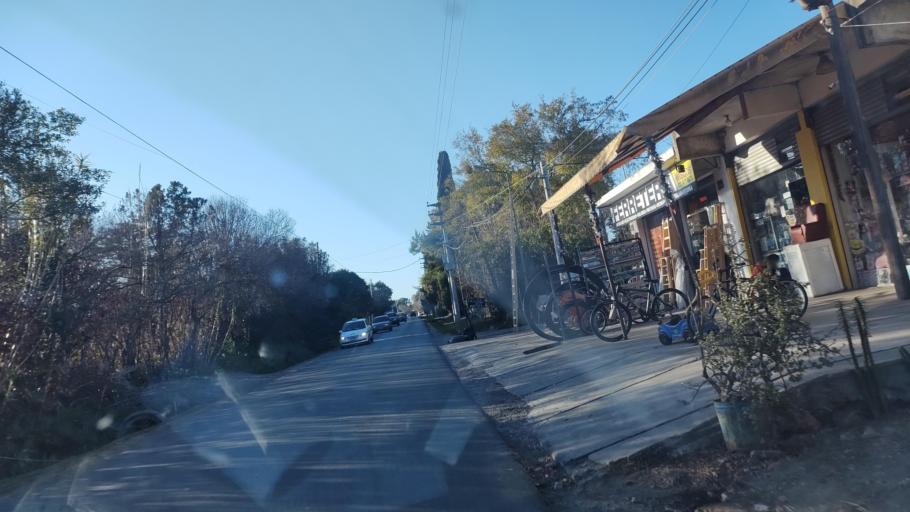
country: AR
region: Buenos Aires
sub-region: Partido de La Plata
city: La Plata
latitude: -34.9020
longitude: -58.0539
